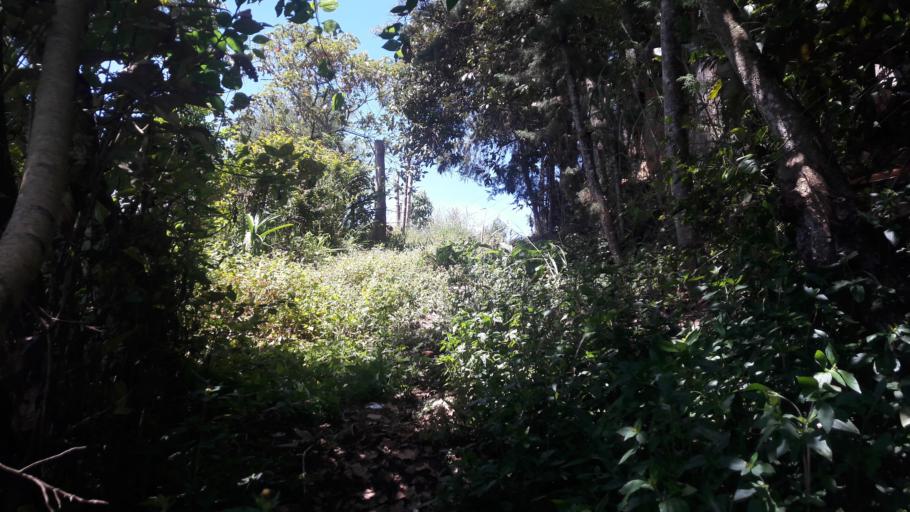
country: CO
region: Cundinamarca
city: Tenza
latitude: 5.0884
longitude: -73.4134
